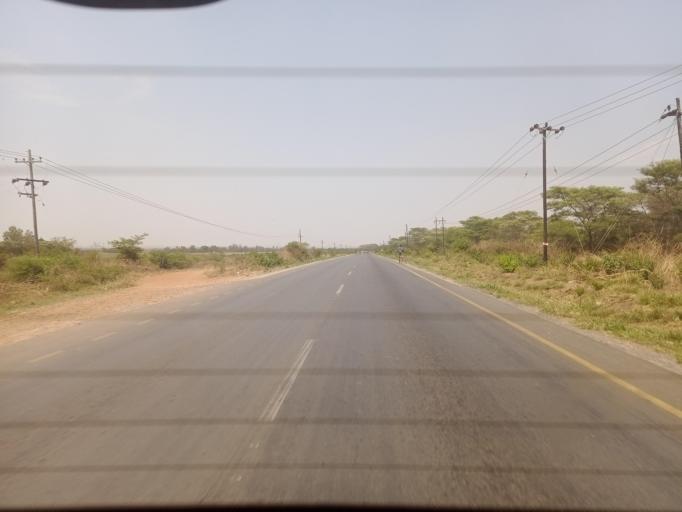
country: ZM
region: Lusaka
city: Lusaka
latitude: -15.2681
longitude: 28.4179
